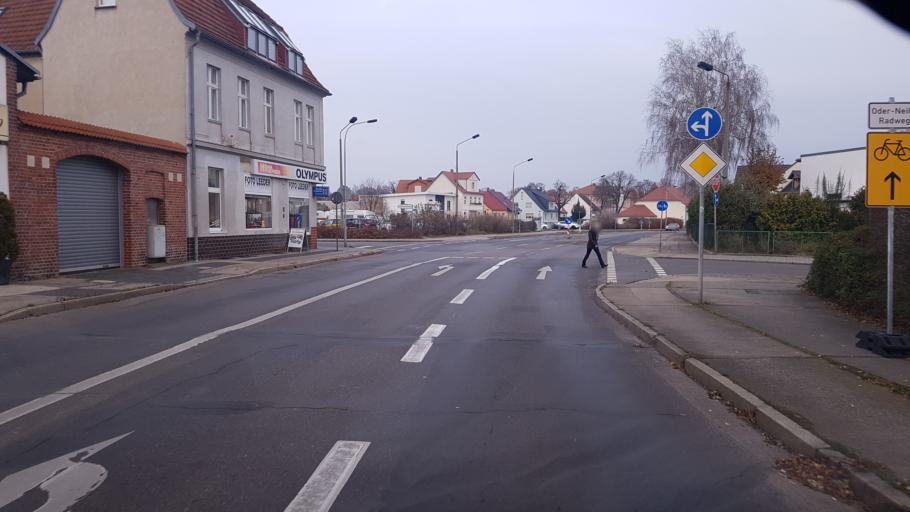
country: DE
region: Brandenburg
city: Eisenhuettenstadt
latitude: 52.1444
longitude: 14.6694
